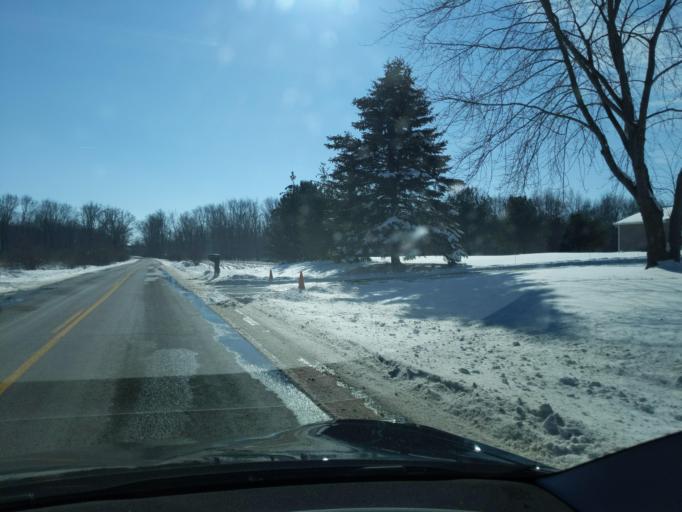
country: US
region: Michigan
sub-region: Ingham County
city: Stockbridge
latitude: 42.5135
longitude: -84.0730
